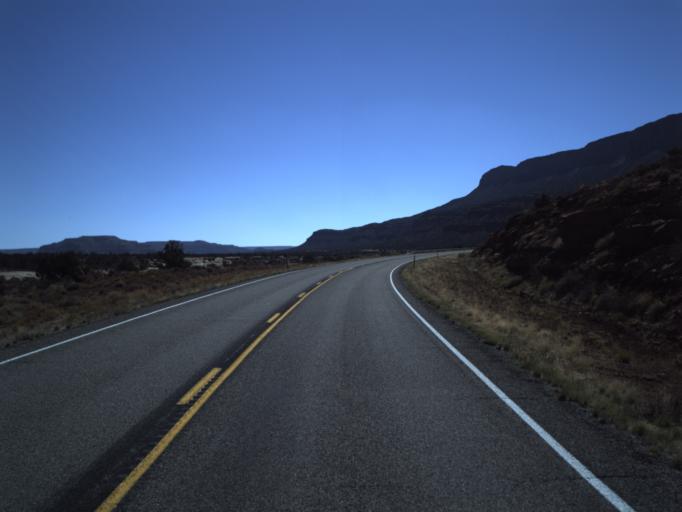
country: US
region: Utah
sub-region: San Juan County
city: Blanding
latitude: 37.6903
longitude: -110.2255
